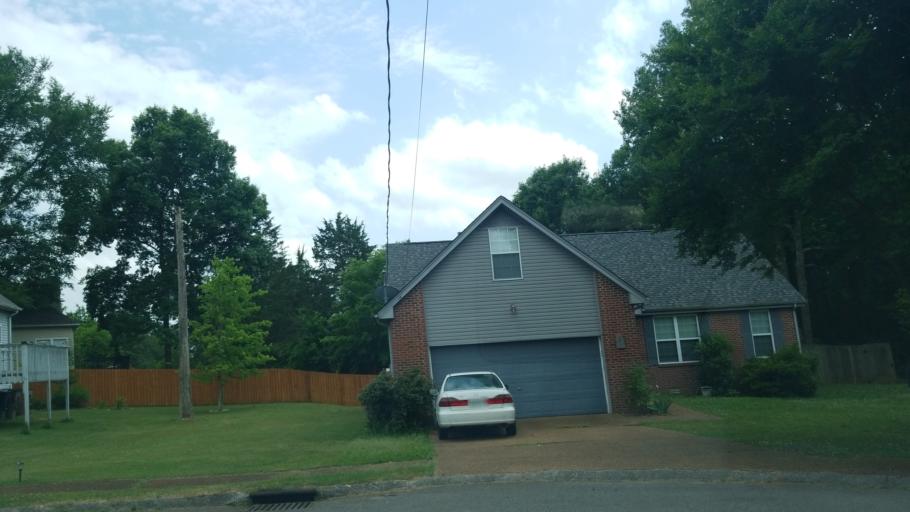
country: US
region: Tennessee
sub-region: Rutherford County
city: La Vergne
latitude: 36.0685
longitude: -86.6014
